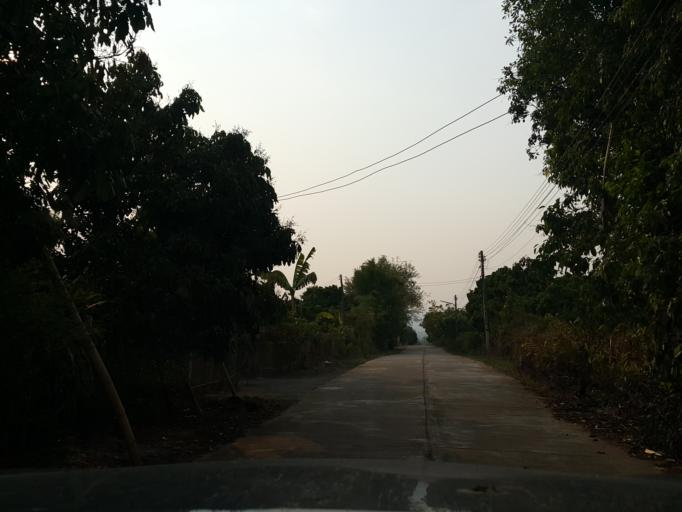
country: TH
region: Lamphun
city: Li
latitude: 17.8100
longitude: 98.9478
